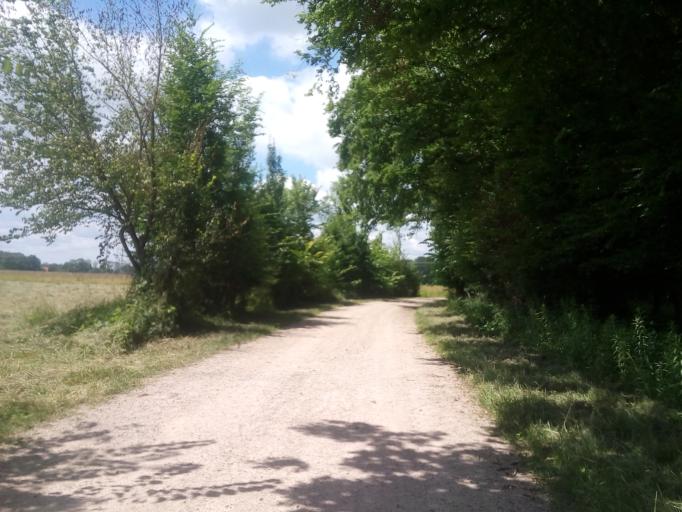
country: DE
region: Baden-Wuerttemberg
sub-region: Freiburg Region
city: Rheinau
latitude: 48.6435
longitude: 7.9452
